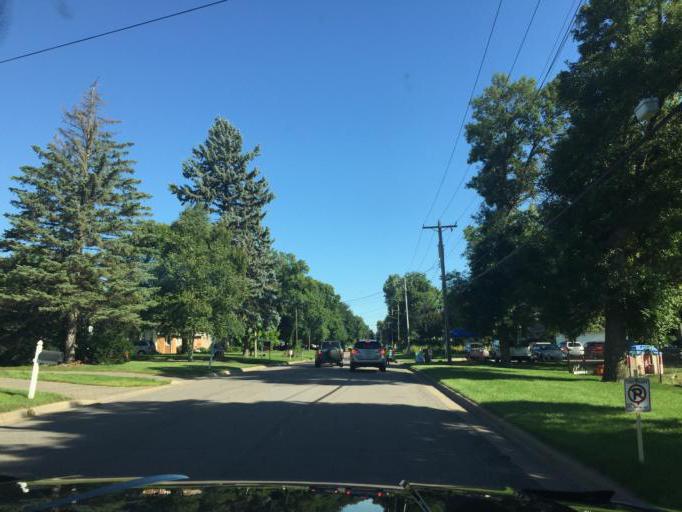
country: US
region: Minnesota
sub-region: Ramsey County
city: Roseville
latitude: 44.9925
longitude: -93.1413
